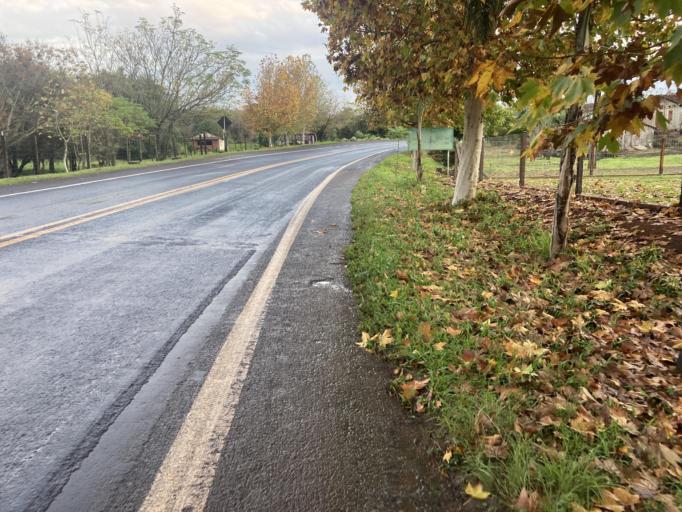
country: BR
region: Rio Grande do Sul
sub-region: Sao Pedro Do Butia
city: Butia Inferior
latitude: -27.9913
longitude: -54.8324
